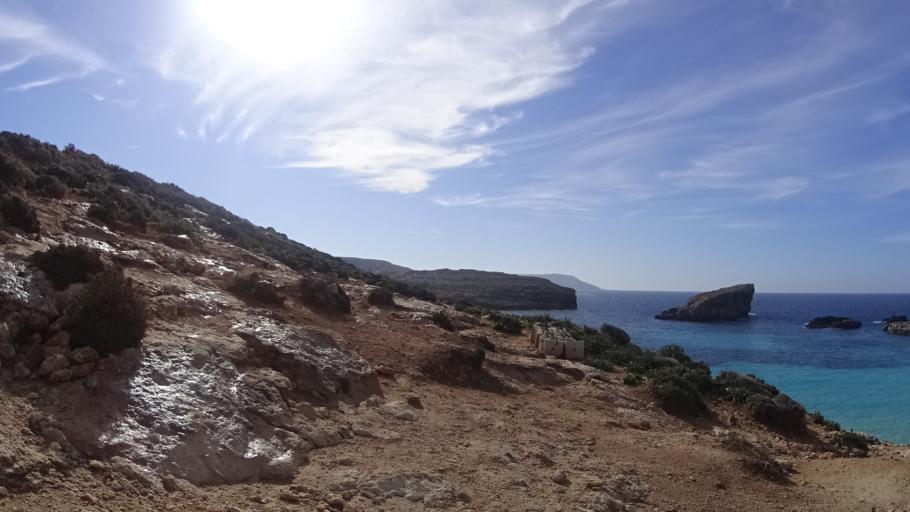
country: MT
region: Il-Qala
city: Qala
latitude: 36.0135
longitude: 14.3242
